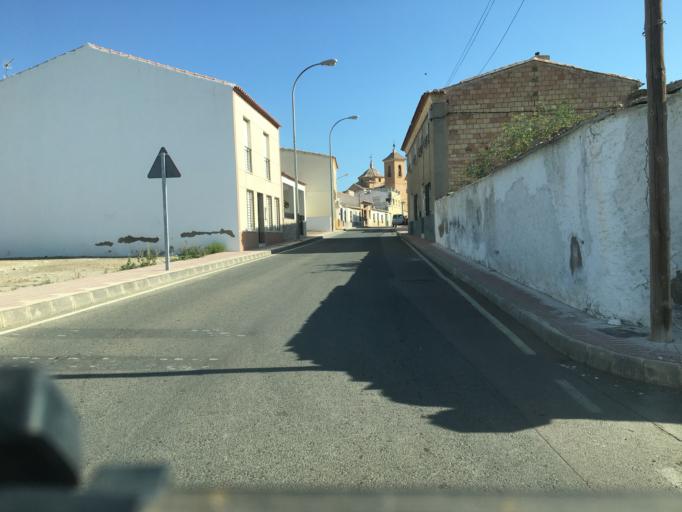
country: ES
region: Andalusia
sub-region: Provincia de Almeria
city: Huercal-Overa
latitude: 37.4607
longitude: -1.9894
